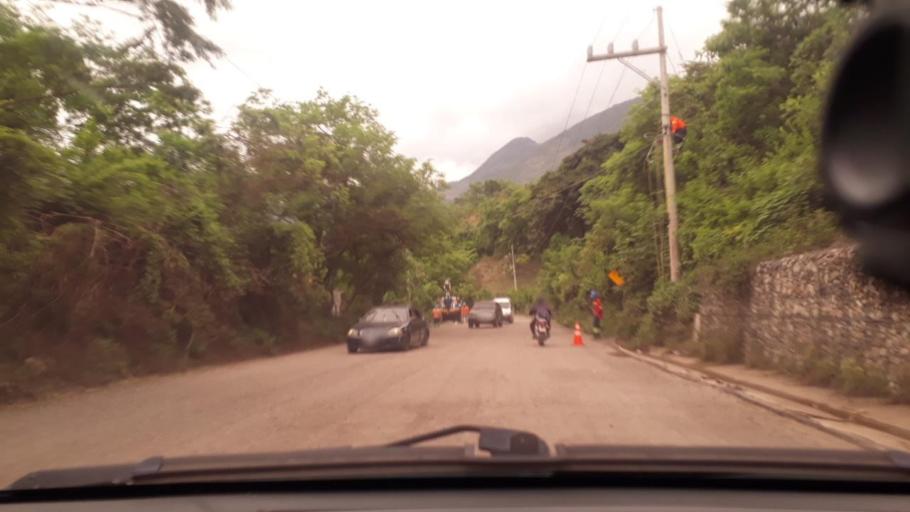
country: GT
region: Chiquimula
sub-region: Municipio de San Juan Ermita
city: San Juan Ermita
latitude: 14.7530
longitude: -89.4485
